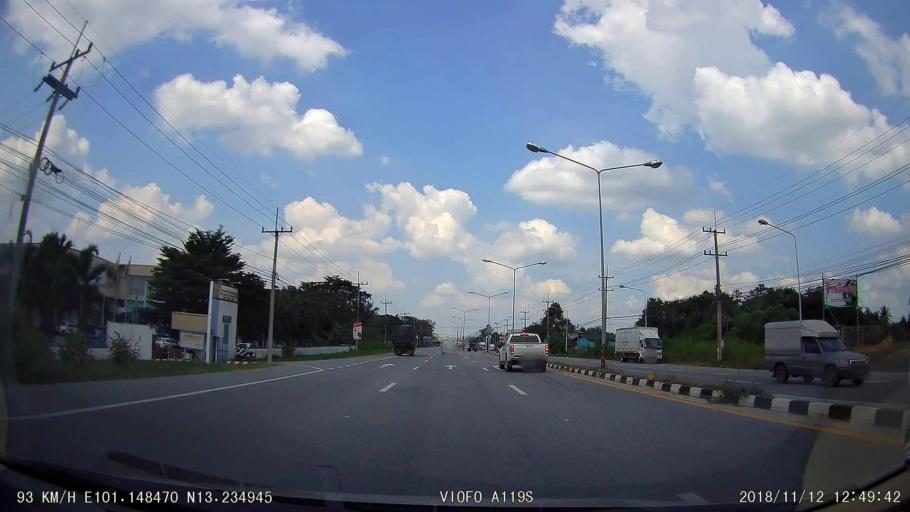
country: TH
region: Chon Buri
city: Ban Bueng
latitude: 13.2352
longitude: 101.1484
